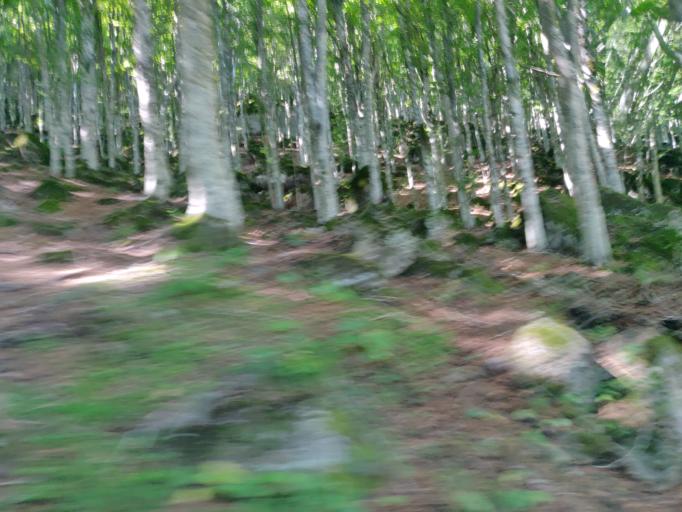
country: IT
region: Tuscany
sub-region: Provincia di Siena
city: Abbadia San Salvatore
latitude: 42.8953
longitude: 11.6292
